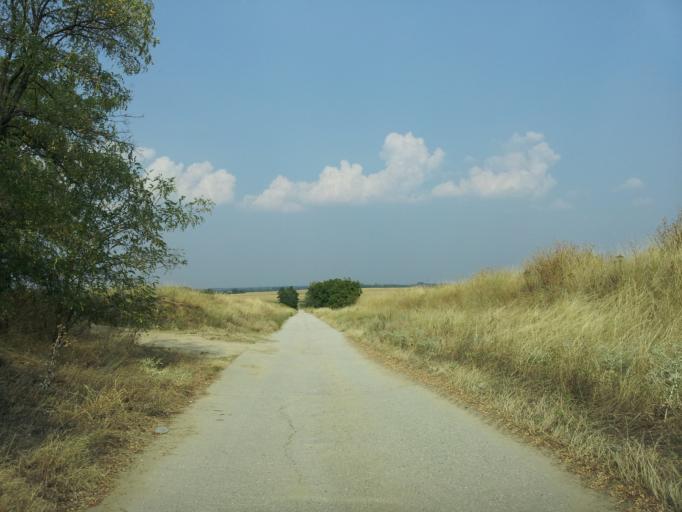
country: HU
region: Gyor-Moson-Sopron
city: Nyul
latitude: 47.6069
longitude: 17.6988
